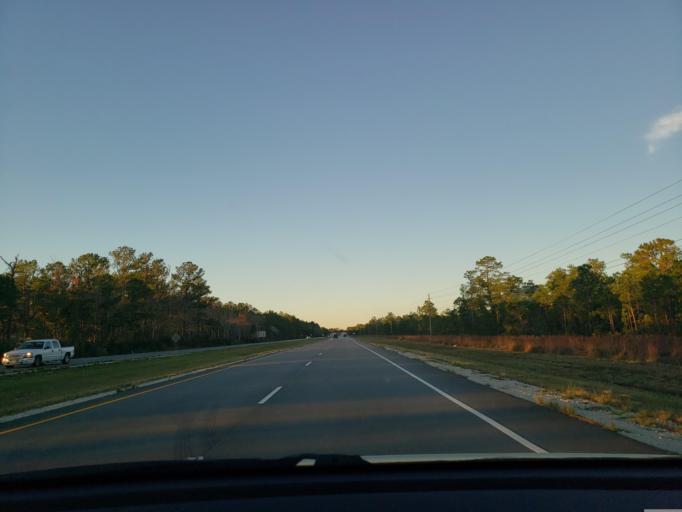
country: US
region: North Carolina
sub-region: Onslow County
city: Sneads Ferry
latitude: 34.6013
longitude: -77.4817
